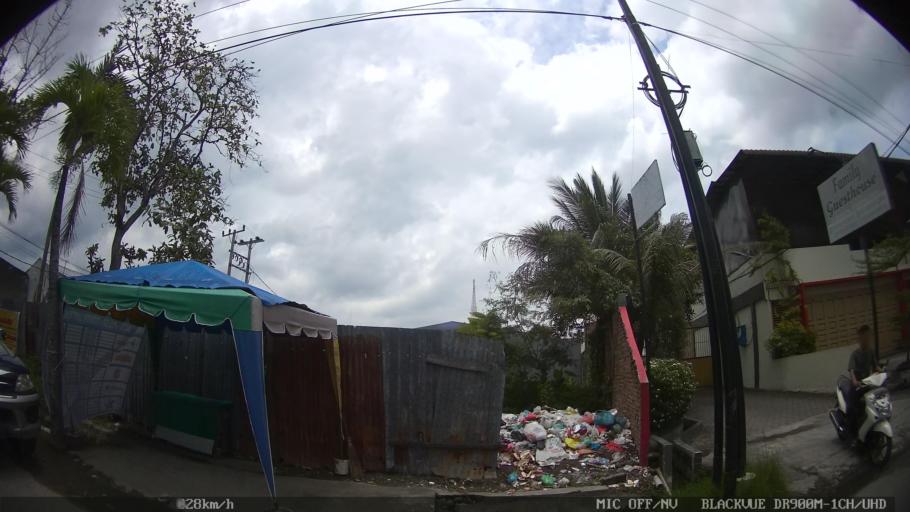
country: ID
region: North Sumatra
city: Medan
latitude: 3.6140
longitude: 98.6478
